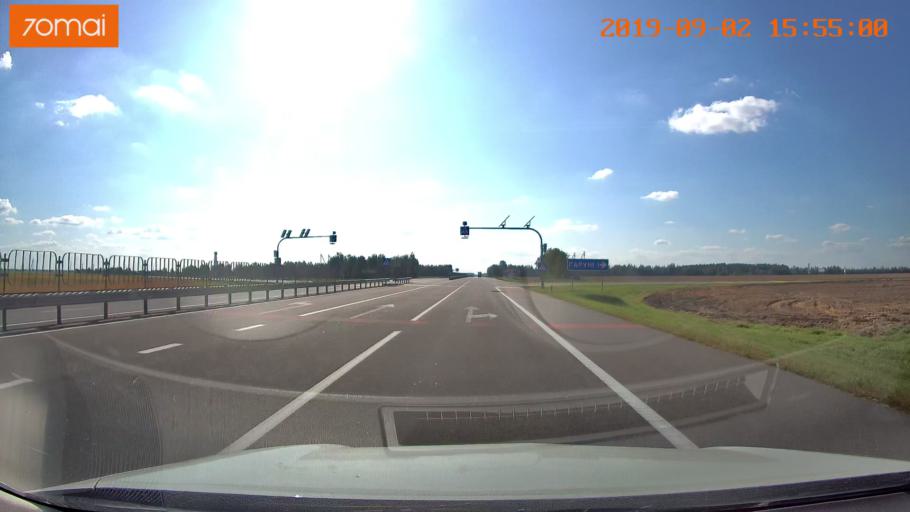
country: BY
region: Minsk
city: Byerazino
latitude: 53.8504
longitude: 29.1102
